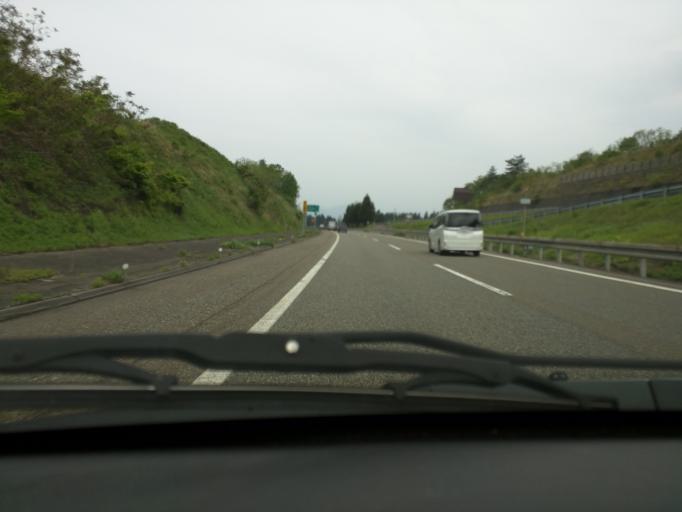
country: JP
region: Niigata
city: Ojiya
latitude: 37.2703
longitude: 138.8118
